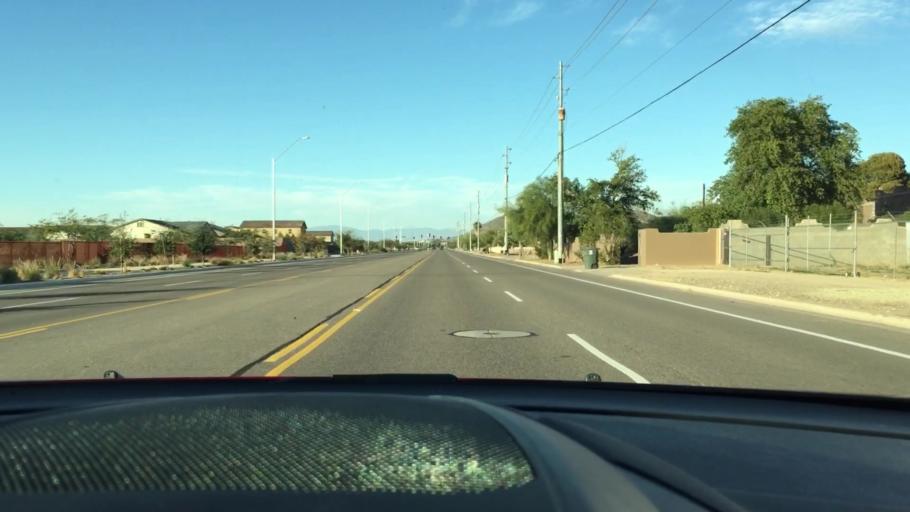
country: US
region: Arizona
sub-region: Maricopa County
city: Sun City
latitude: 33.6851
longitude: -112.2550
